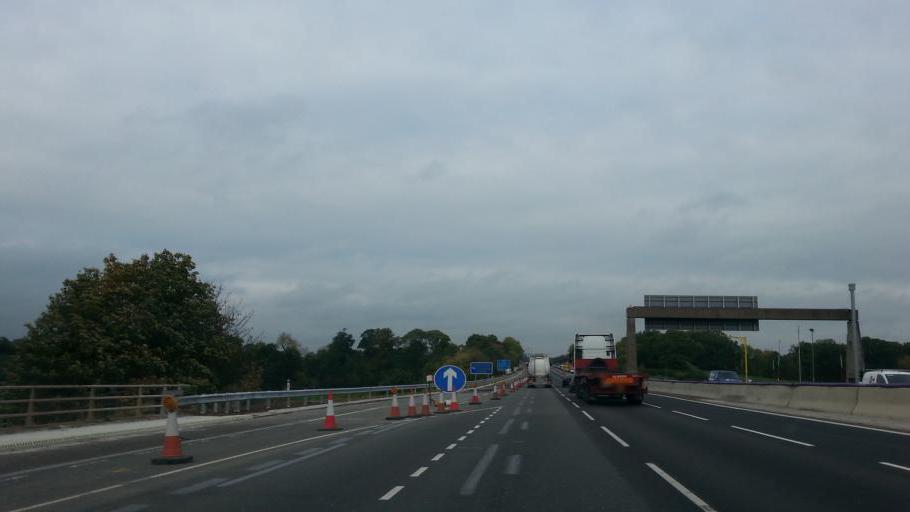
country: GB
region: England
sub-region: Cheshire East
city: Holmes Chapel
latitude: 53.2055
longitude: -2.3880
